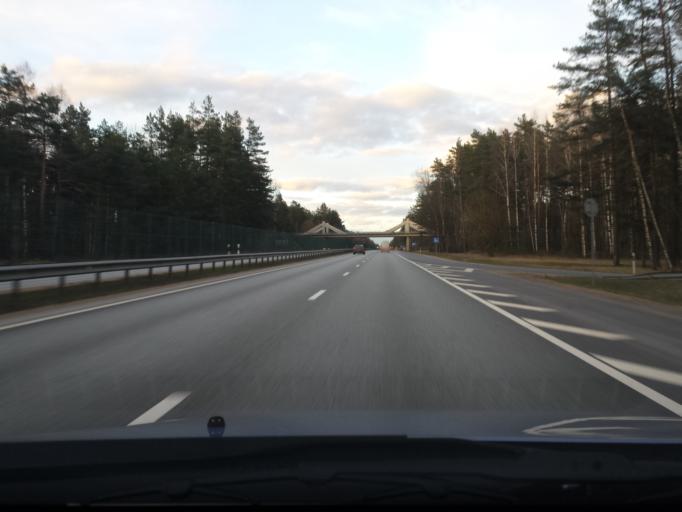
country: LV
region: Riga
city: Bergi
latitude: 57.0087
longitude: 24.3040
